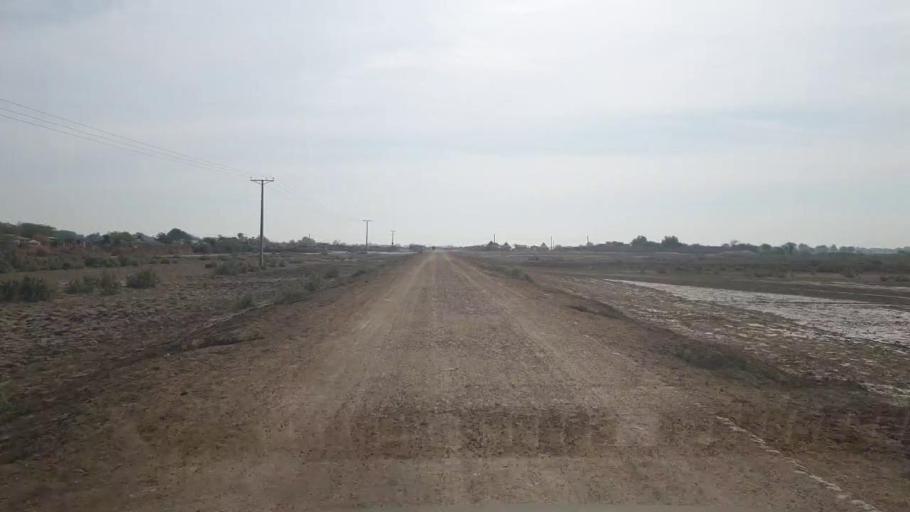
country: PK
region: Sindh
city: Umarkot
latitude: 25.3604
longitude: 69.6512
